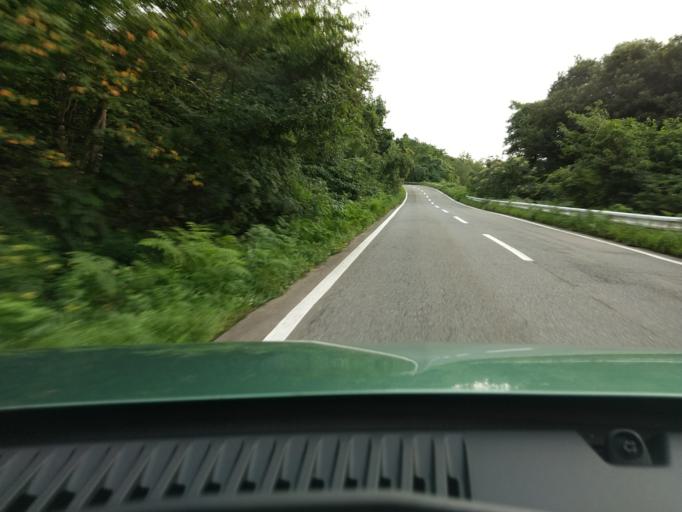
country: JP
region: Akita
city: Akita
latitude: 39.7568
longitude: 140.1601
